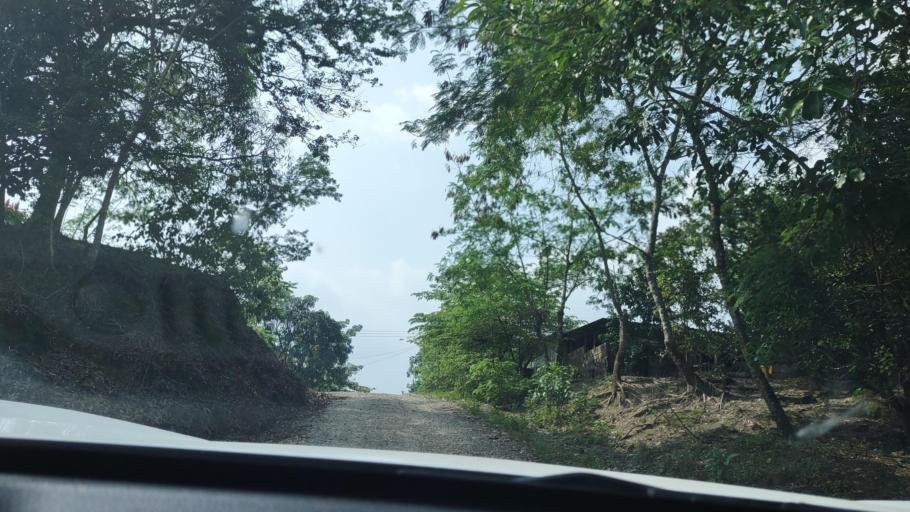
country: MX
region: Veracruz
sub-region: Uxpanapa
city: Poblado 10
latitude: 17.5462
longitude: -94.2911
